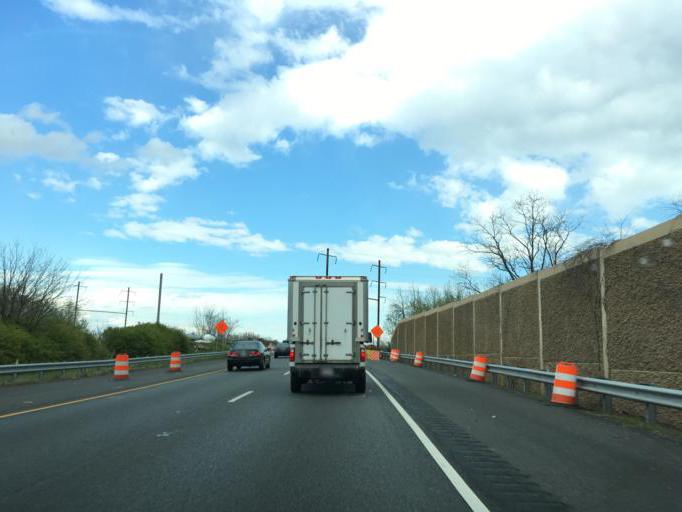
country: US
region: Maryland
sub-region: Baltimore County
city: Essex
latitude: 39.3135
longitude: -76.4950
